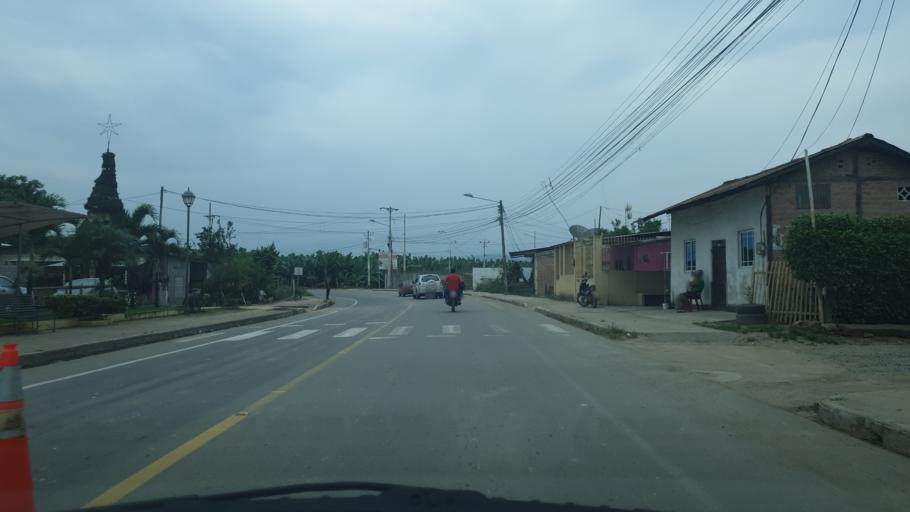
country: EC
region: El Oro
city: Pasaje
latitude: -3.3627
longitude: -79.8411
